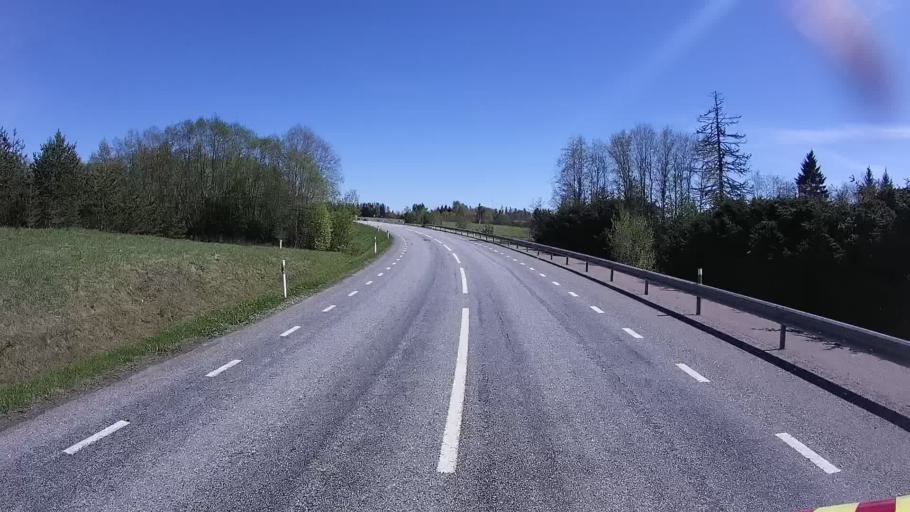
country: EE
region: Laeaene-Virumaa
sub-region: Tapa vald
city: Tapa
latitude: 59.2524
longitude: 25.6736
